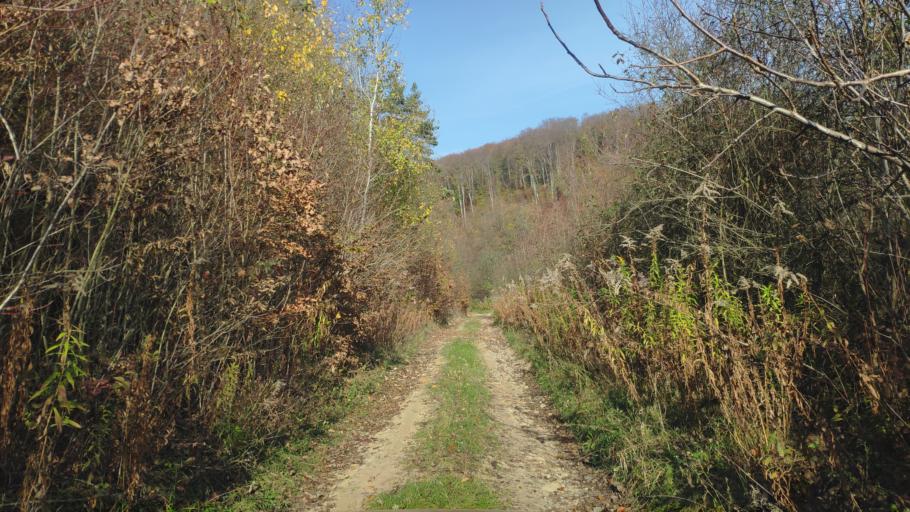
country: SK
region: Presovsky
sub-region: Okres Presov
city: Presov
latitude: 48.9020
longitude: 21.2220
